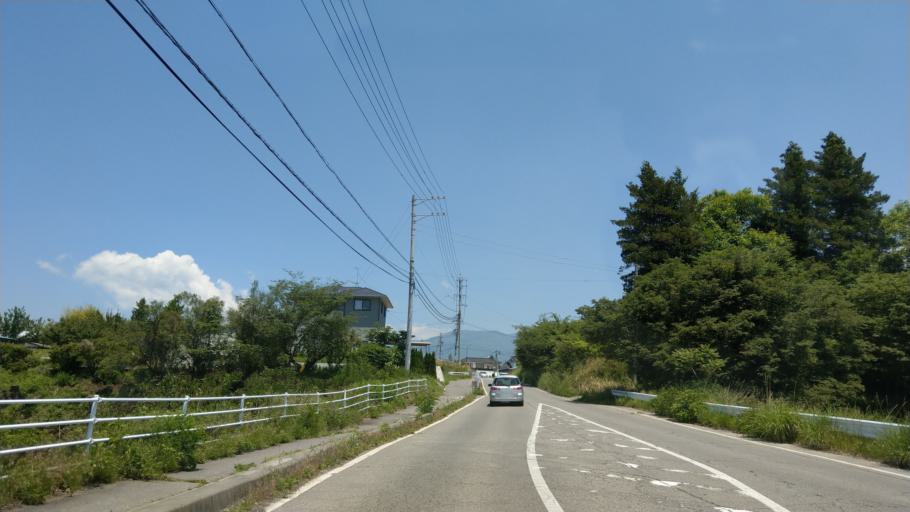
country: JP
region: Nagano
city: Komoro
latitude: 36.2942
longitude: 138.4398
